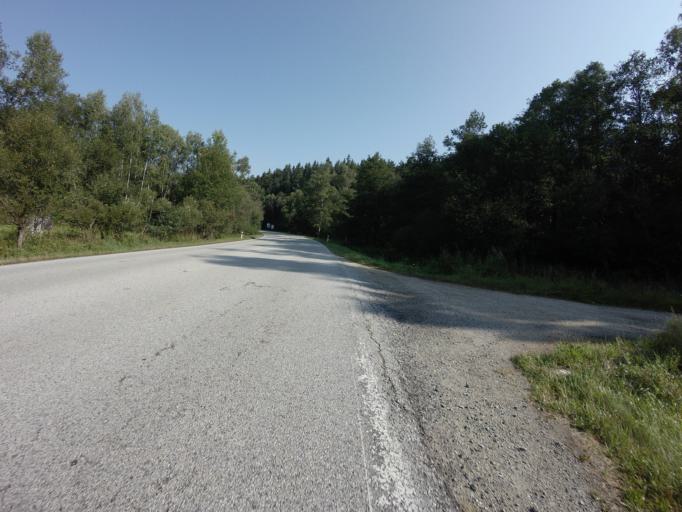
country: CZ
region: Jihocesky
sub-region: Okres Cesky Krumlov
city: Vyssi Brod
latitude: 48.5735
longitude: 14.3215
